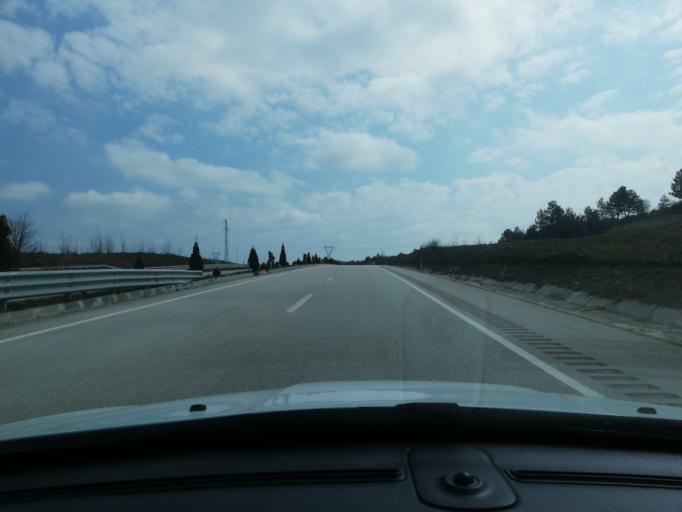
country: TR
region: Kastamonu
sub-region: Cide
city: Kastamonu
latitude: 41.3751
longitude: 33.7942
